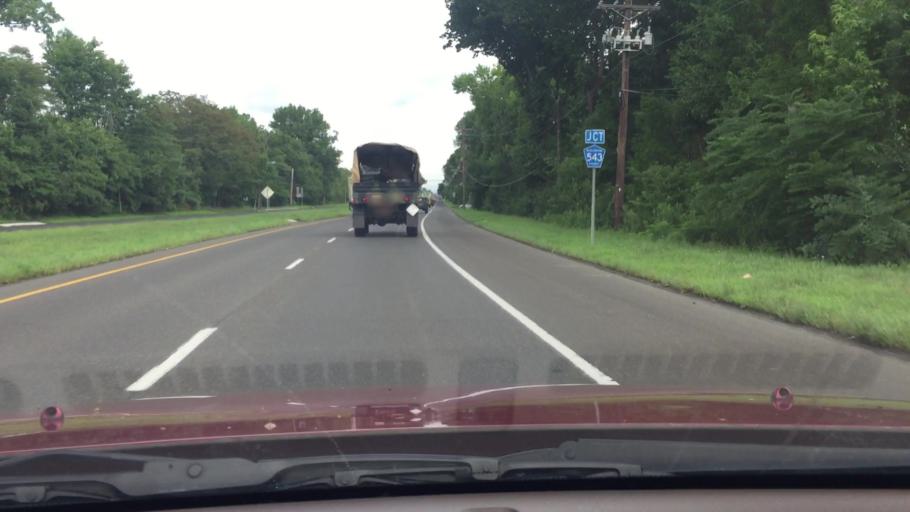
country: US
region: New Jersey
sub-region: Burlington County
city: Fort Dix
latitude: 40.0743
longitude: -74.6594
